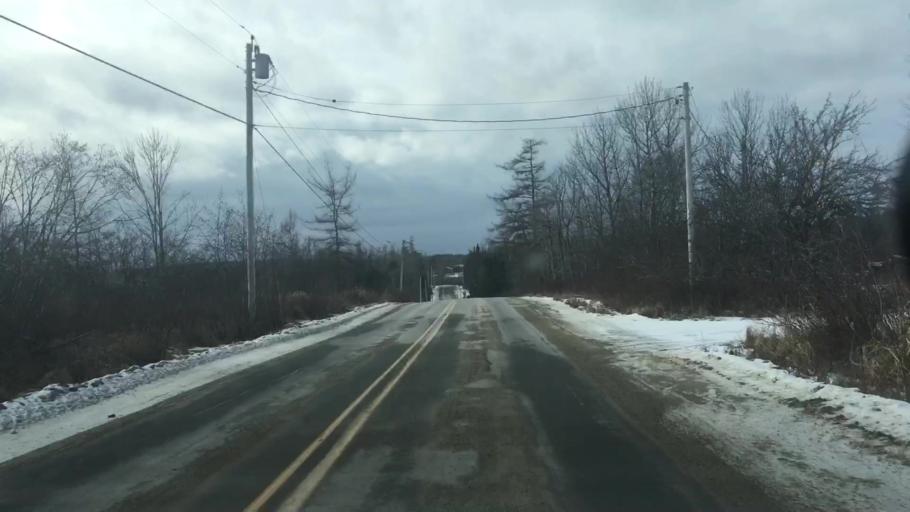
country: US
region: Maine
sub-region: Washington County
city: Machias
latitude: 44.6560
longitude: -67.5237
